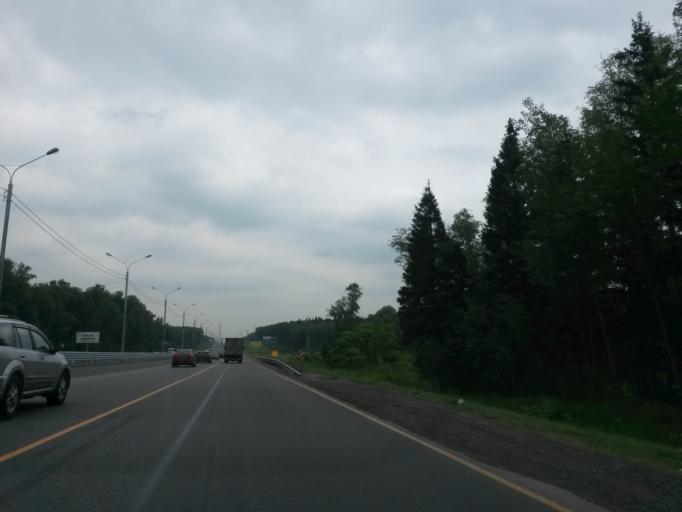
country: RU
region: Moskovskaya
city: Lyubuchany
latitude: 55.2646
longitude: 37.5355
